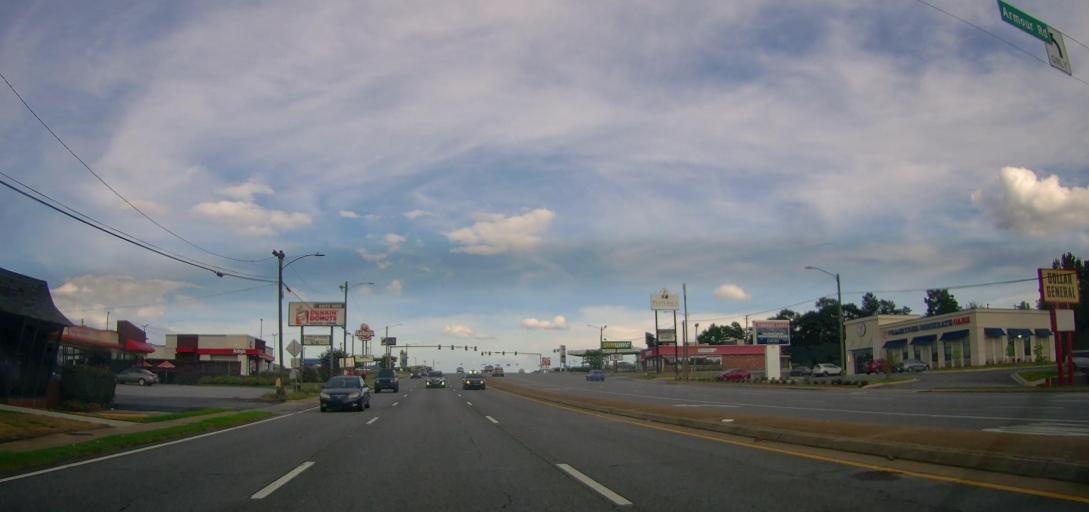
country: US
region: Georgia
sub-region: Muscogee County
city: Columbus
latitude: 32.5071
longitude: -84.9555
